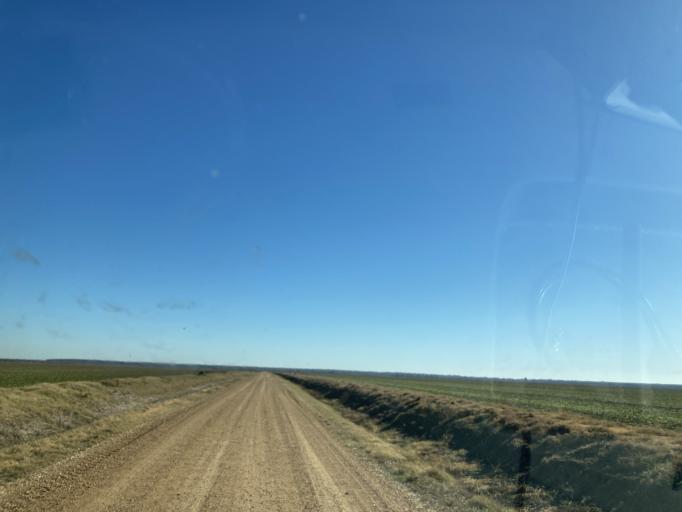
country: US
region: Mississippi
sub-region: Sharkey County
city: Rolling Fork
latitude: 32.8498
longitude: -90.6955
